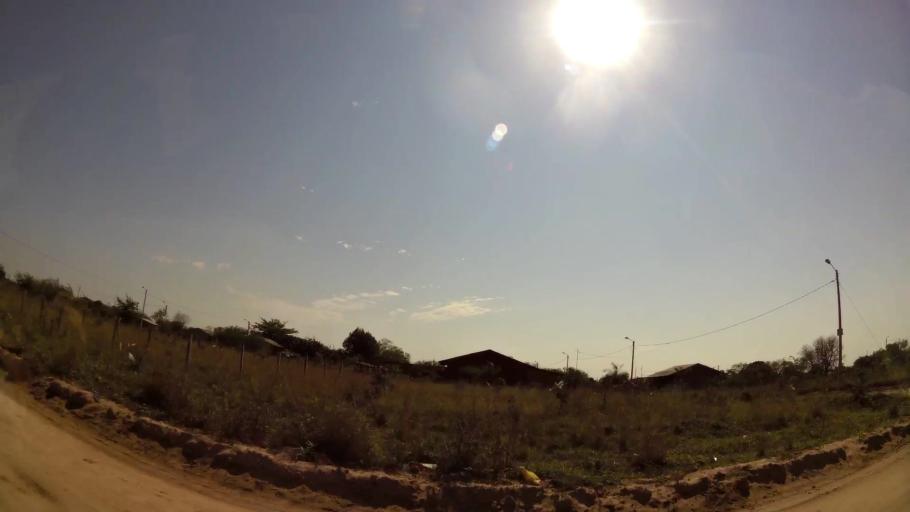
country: BO
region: Santa Cruz
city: Cotoca
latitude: -17.7168
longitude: -63.0656
